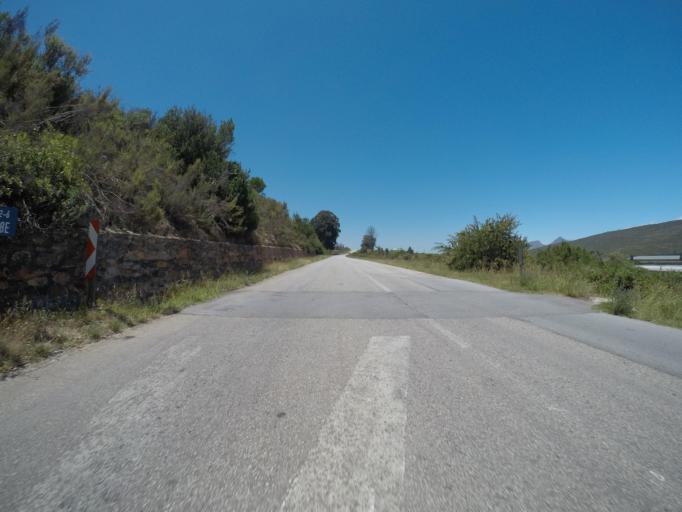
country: ZA
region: Western Cape
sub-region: Eden District Municipality
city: Plettenberg Bay
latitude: -33.8139
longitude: 23.7808
